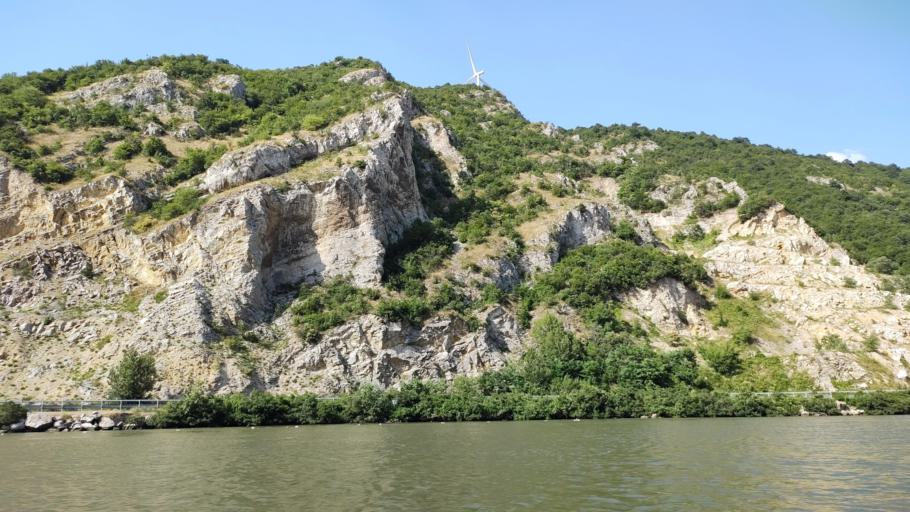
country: RO
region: Caras-Severin
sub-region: Comuna Pescari
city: Coronini
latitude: 44.6547
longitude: 21.7174
